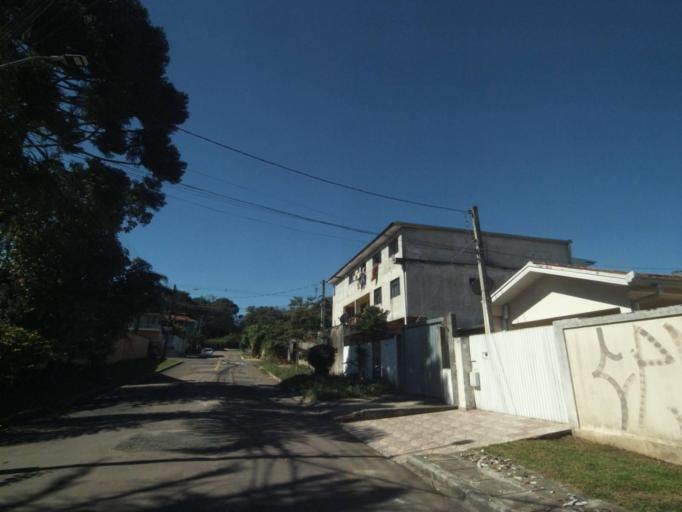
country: BR
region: Parana
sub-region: Curitiba
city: Curitiba
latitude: -25.4552
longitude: -49.3514
